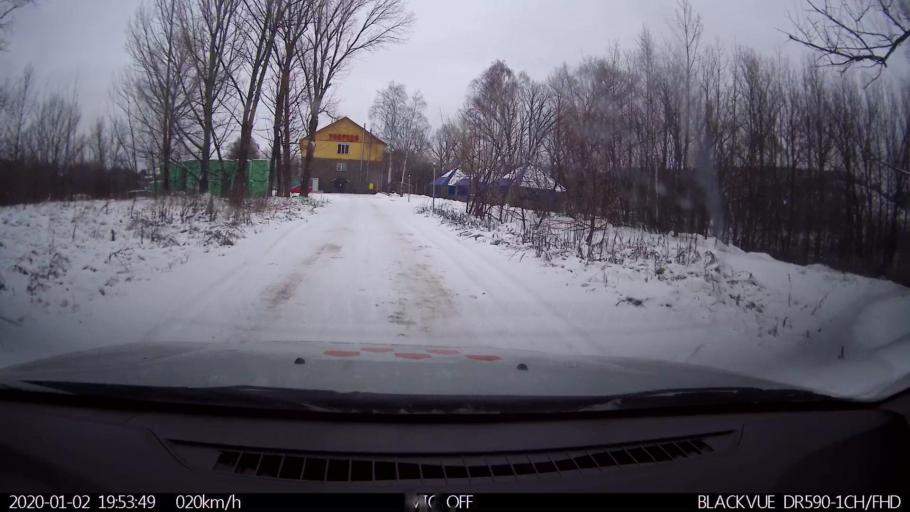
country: RU
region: Nizjnij Novgorod
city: Nizhniy Novgorod
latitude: 56.2751
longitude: 43.9595
